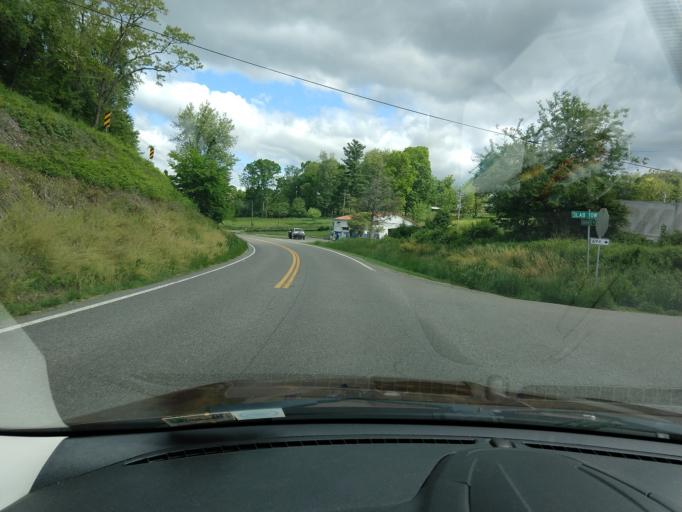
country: US
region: Virginia
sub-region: Wythe County
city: Wytheville
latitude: 36.8454
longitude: -80.9715
